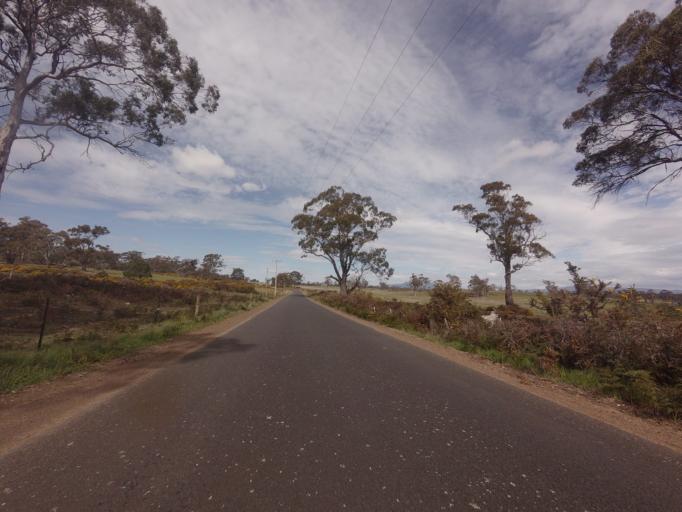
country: AU
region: Tasmania
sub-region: Northern Midlands
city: Longford
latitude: -41.7198
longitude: 147.1879
